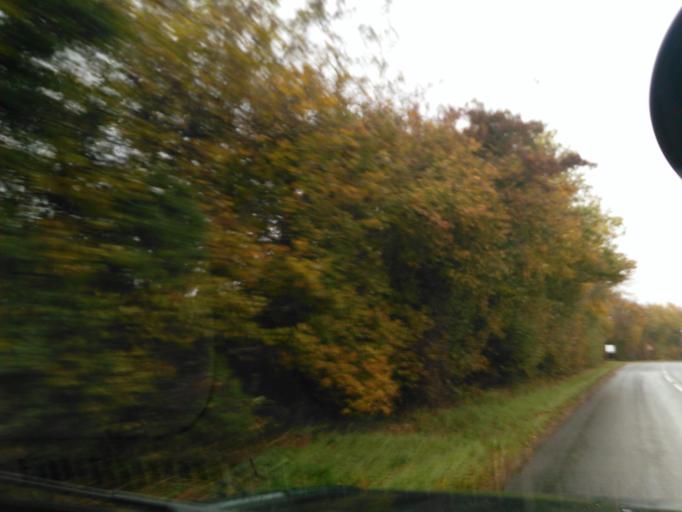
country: GB
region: England
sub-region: Wiltshire
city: Box
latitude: 51.3973
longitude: -2.2312
